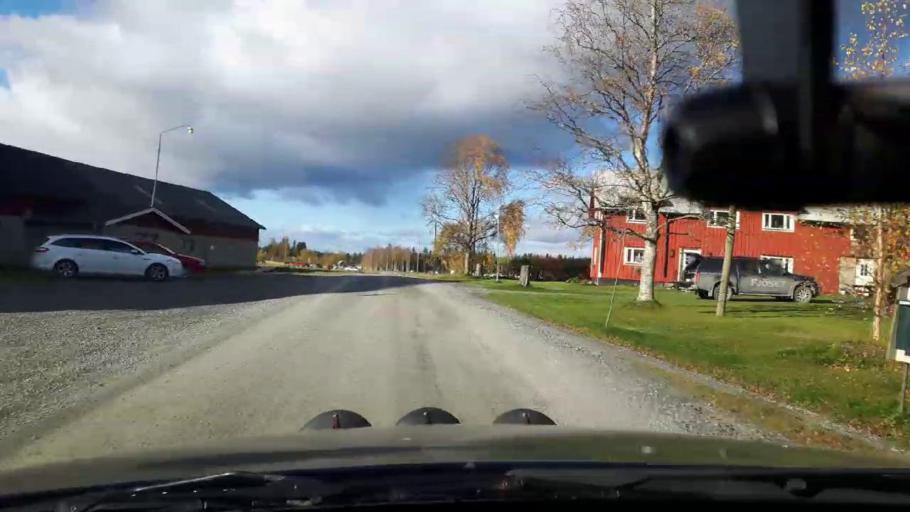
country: SE
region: Jaemtland
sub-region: Bergs Kommun
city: Hoverberg
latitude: 63.0602
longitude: 14.2344
